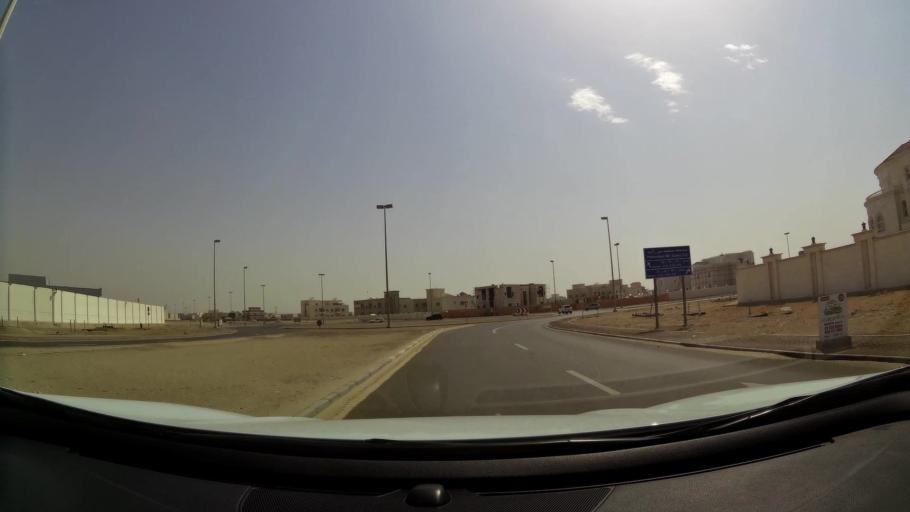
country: AE
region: Abu Dhabi
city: Abu Dhabi
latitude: 24.3164
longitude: 54.5521
